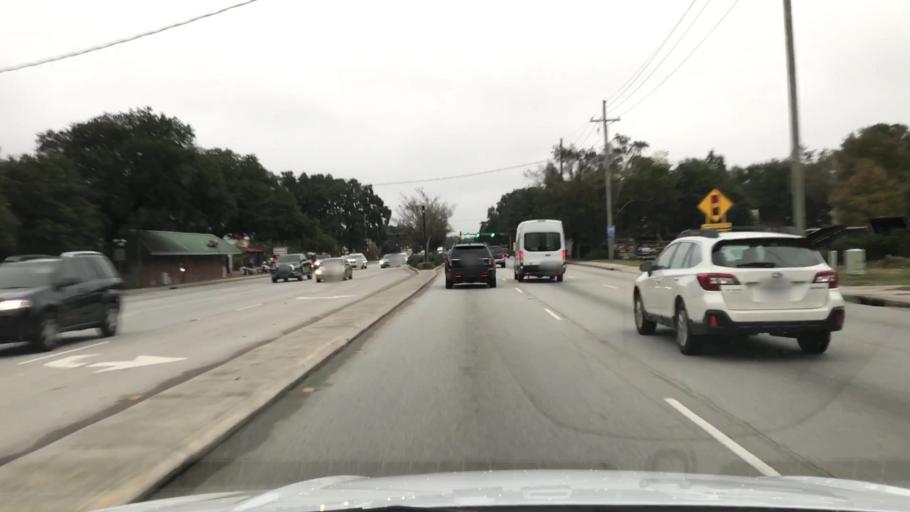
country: US
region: South Carolina
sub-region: Charleston County
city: Mount Pleasant
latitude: 32.8220
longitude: -79.8411
